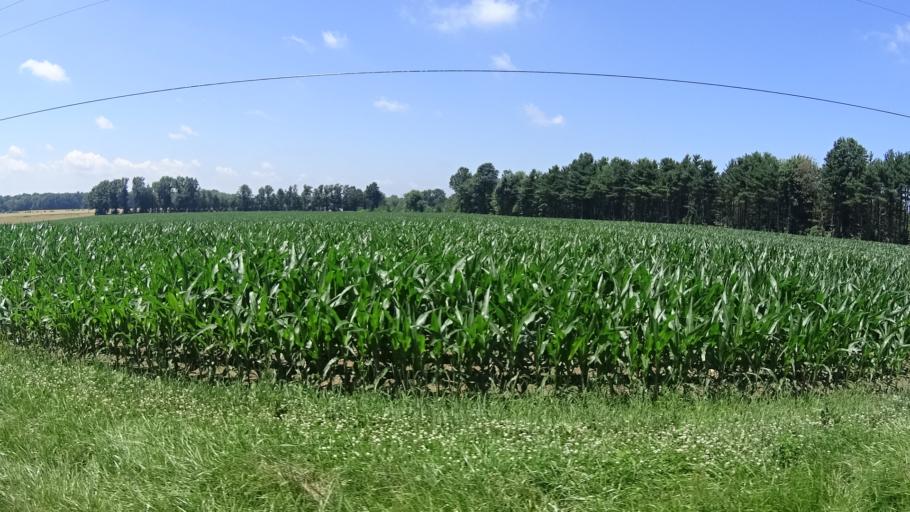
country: US
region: Ohio
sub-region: Huron County
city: Wakeman
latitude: 41.3323
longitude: -82.4091
